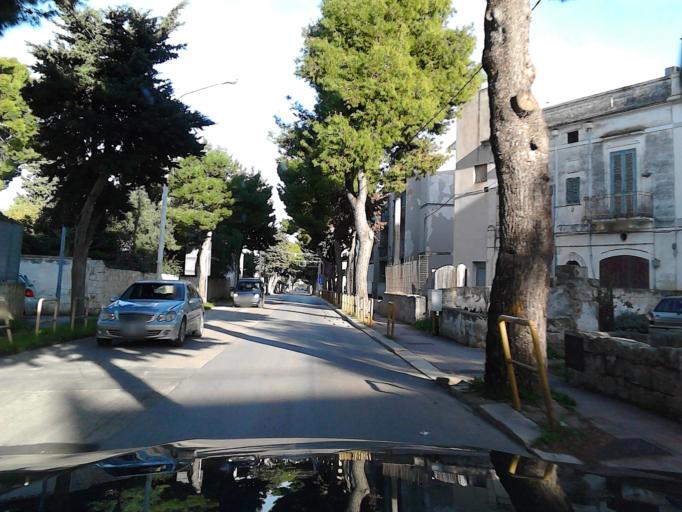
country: IT
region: Apulia
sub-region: Provincia di Bari
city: Mola di Bari
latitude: 41.0536
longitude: 17.0786
